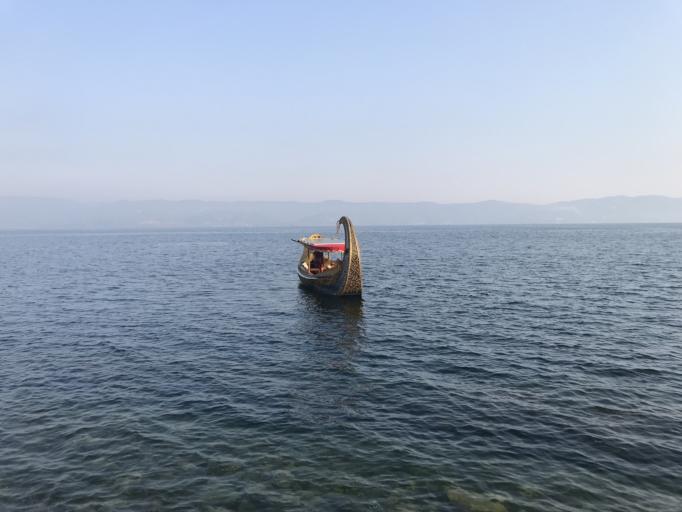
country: TR
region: Sakarya
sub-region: Merkez
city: Sapanca
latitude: 40.6982
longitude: 30.2679
